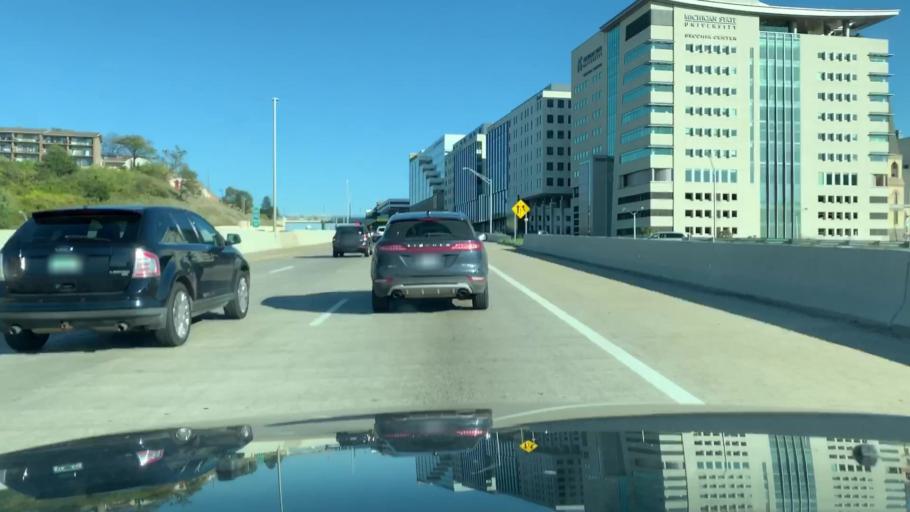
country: US
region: Michigan
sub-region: Kent County
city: Grand Rapids
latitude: 42.9717
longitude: -85.6702
